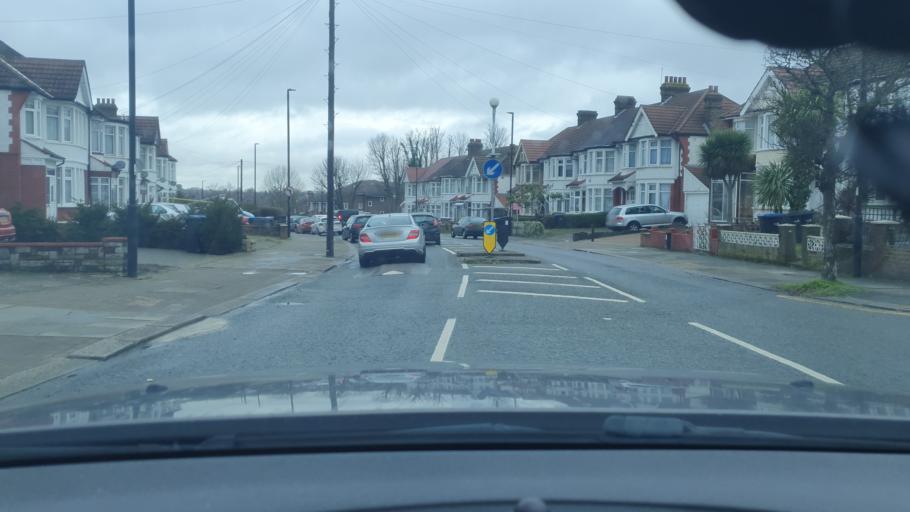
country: GB
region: England
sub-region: Greater London
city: Wood Green
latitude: 51.6089
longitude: -0.1026
